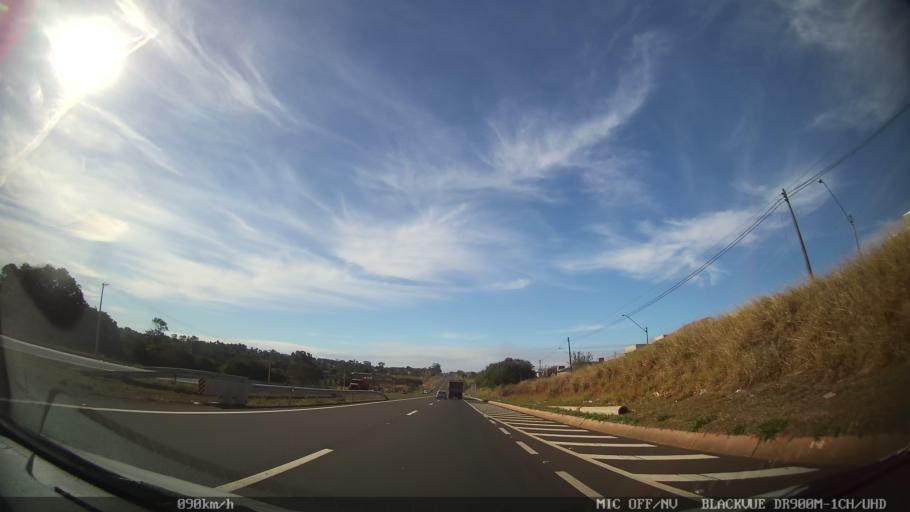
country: BR
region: Sao Paulo
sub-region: Sao Jose Do Rio Preto
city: Sao Jose do Rio Preto
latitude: -20.7557
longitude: -49.3440
